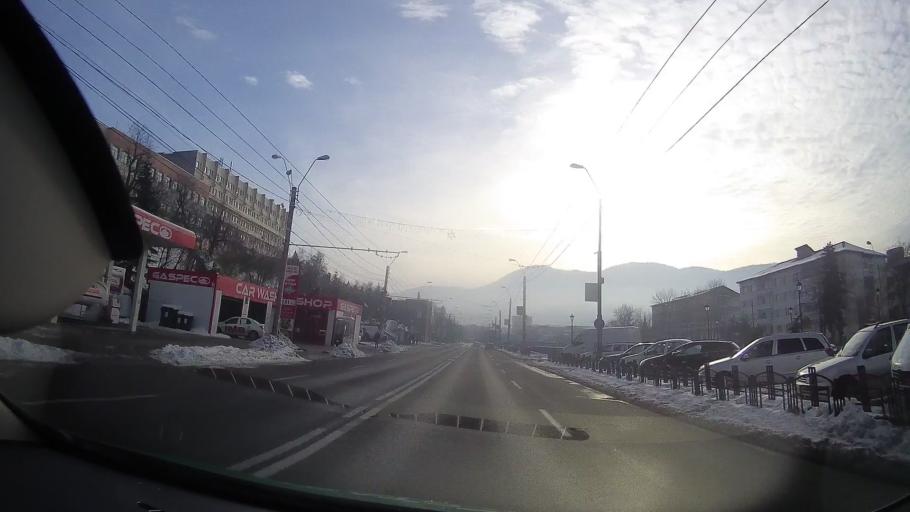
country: RO
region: Neamt
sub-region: Municipiul Piatra-Neamt
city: Valeni
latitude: 46.9298
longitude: 26.3729
